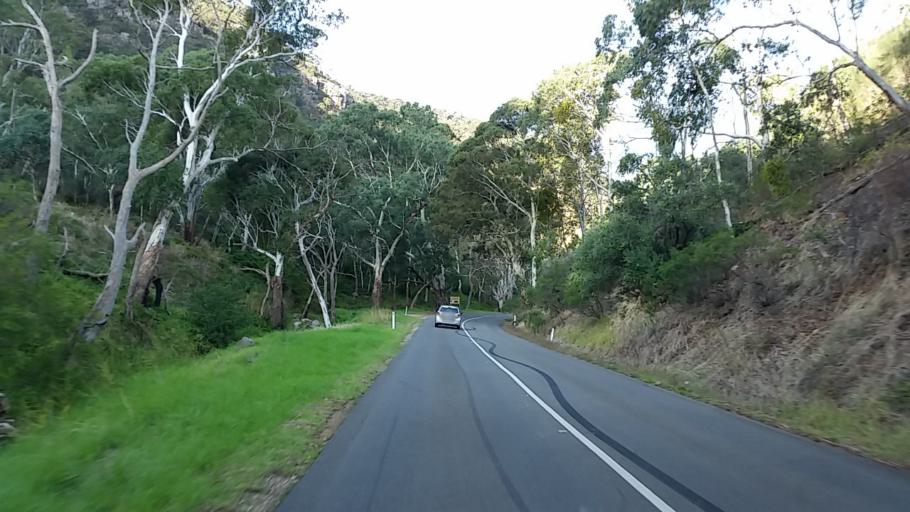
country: AU
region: South Australia
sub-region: Campbelltown
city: Athelstone
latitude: -34.8875
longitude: 138.7114
